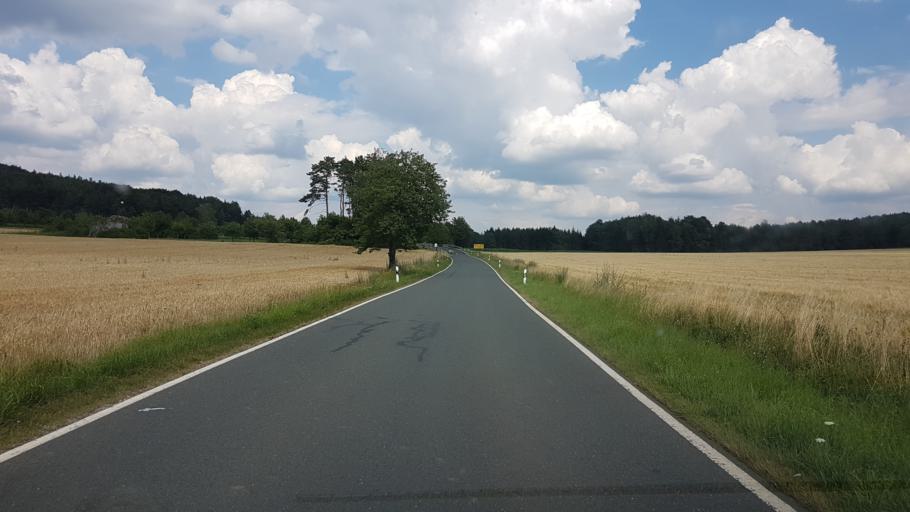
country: DE
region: Bavaria
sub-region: Upper Franconia
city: Egloffstein
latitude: 49.7622
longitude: 11.2683
